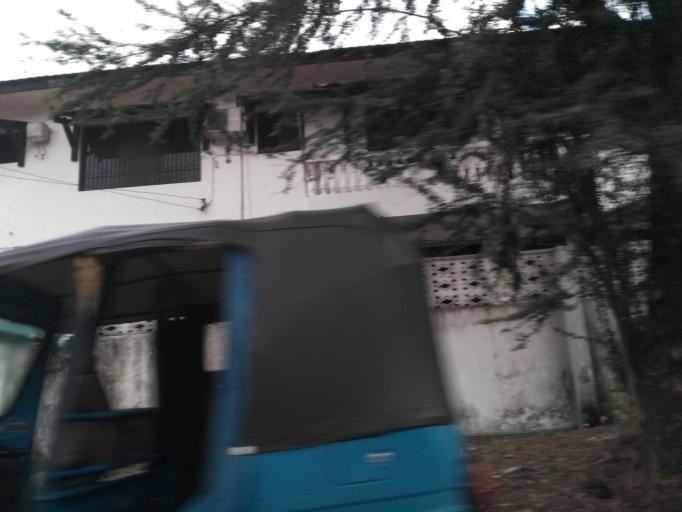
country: TZ
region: Dar es Salaam
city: Magomeni
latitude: -6.7644
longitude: 39.2483
